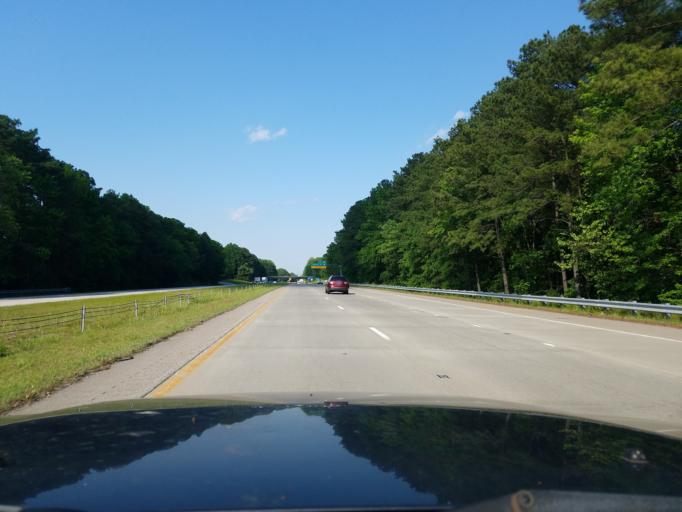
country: US
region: North Carolina
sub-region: Vance County
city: South Henderson
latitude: 36.3312
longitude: -78.4421
